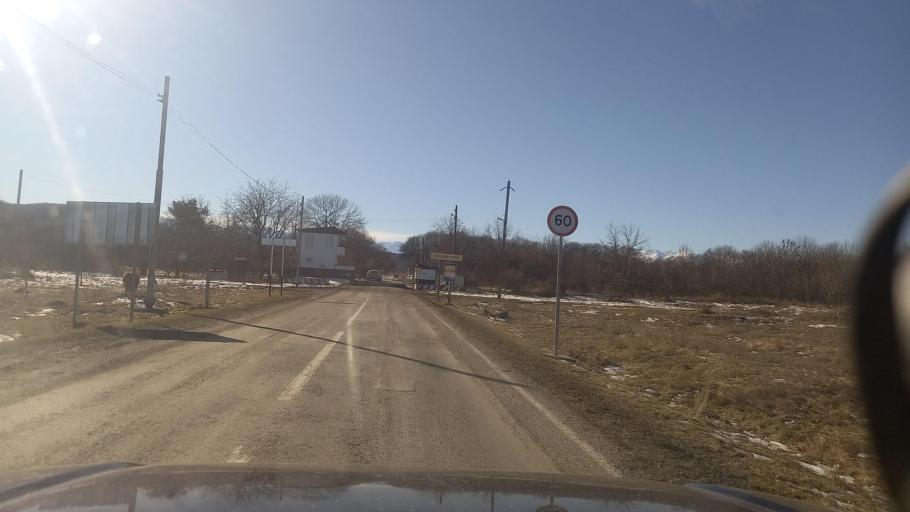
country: RU
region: Kabardino-Balkariya
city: Urukh
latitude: 43.2738
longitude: 43.9981
